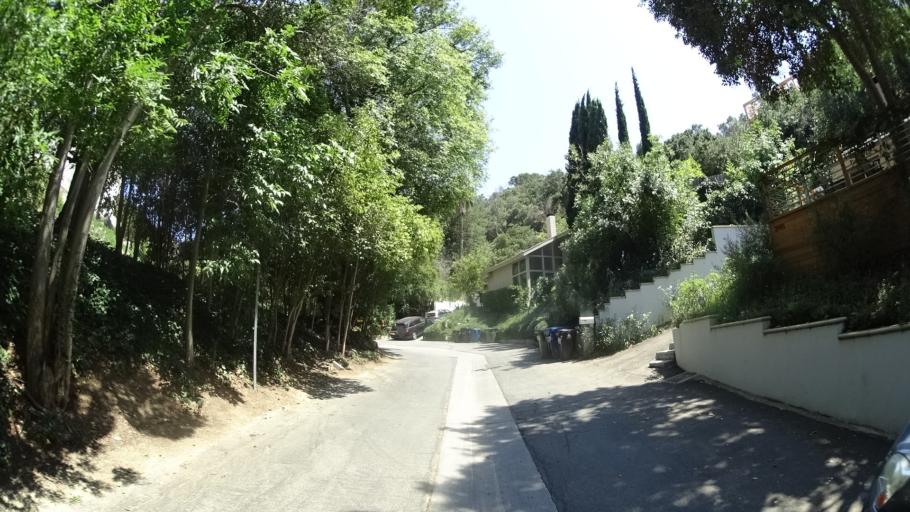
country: US
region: California
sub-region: Los Angeles County
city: Sherman Oaks
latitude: 34.1343
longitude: -118.4091
